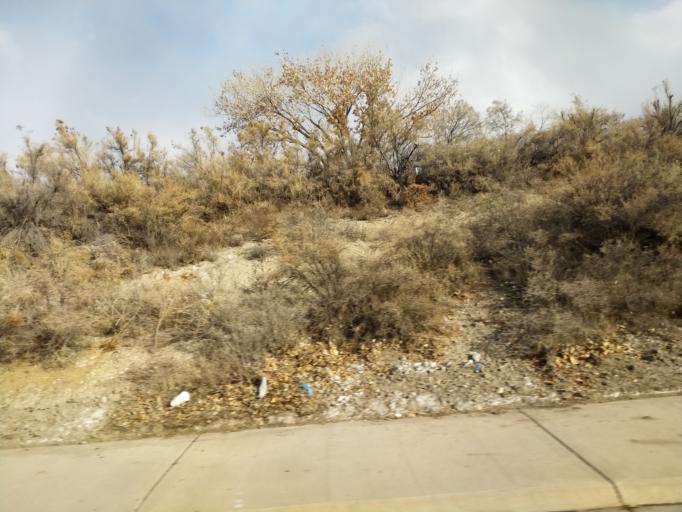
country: US
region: Colorado
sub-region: Mesa County
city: Grand Junction
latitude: 39.0842
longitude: -108.5802
